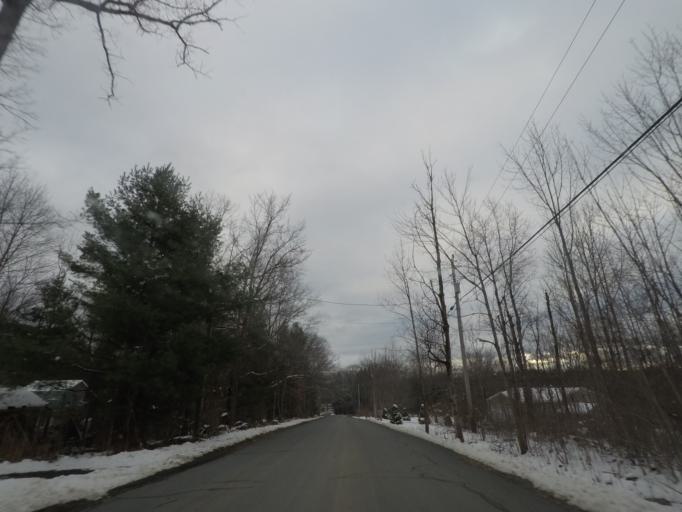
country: US
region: New York
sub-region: Rensselaer County
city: Averill Park
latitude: 42.6483
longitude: -73.5380
